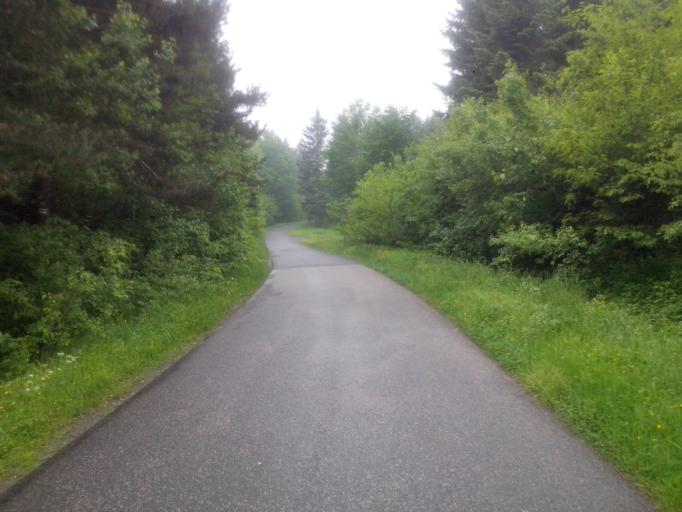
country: PL
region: Subcarpathian Voivodeship
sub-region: Powiat strzyzowski
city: Wysoka Strzyzowska
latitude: 49.8260
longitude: 21.7812
